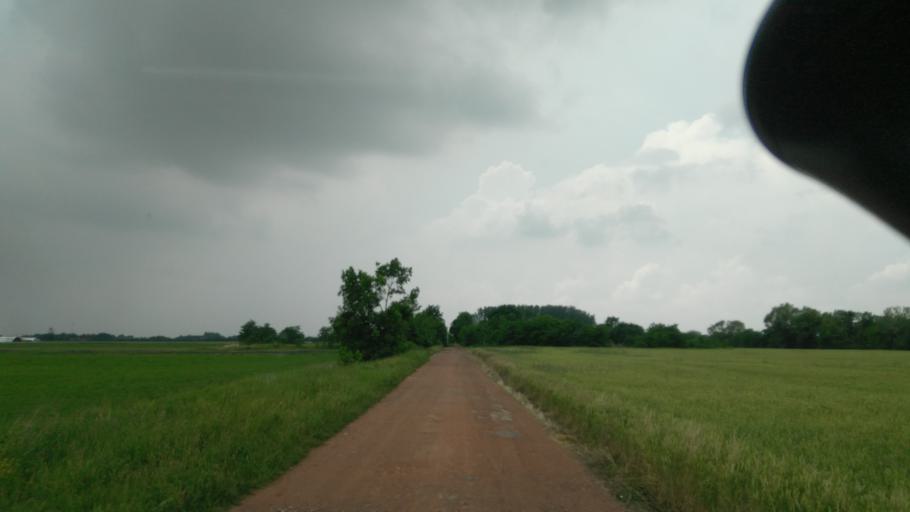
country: HU
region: Bekes
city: Bekescsaba
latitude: 46.7063
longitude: 21.1359
